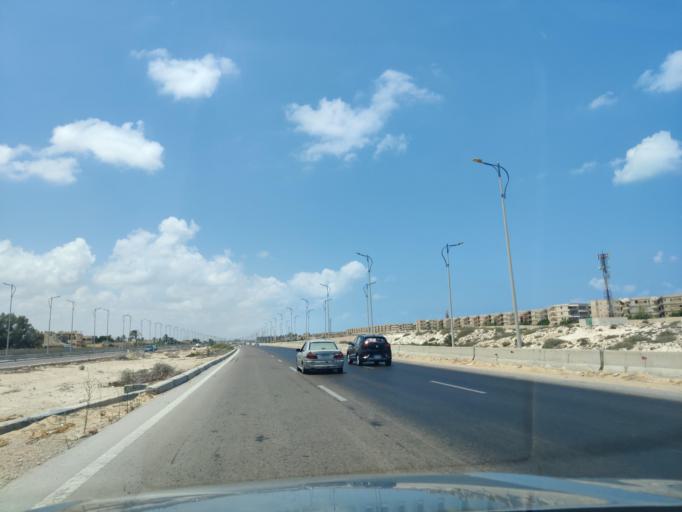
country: EG
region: Muhafazat Matruh
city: Al `Alamayn
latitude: 30.9263
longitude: 29.4679
